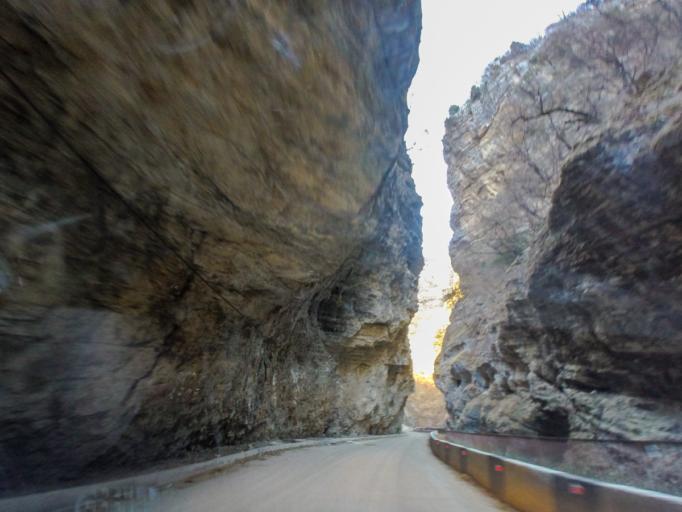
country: RU
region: Kabardino-Balkariya
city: Zhankhoteko
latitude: 43.4213
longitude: 43.2241
